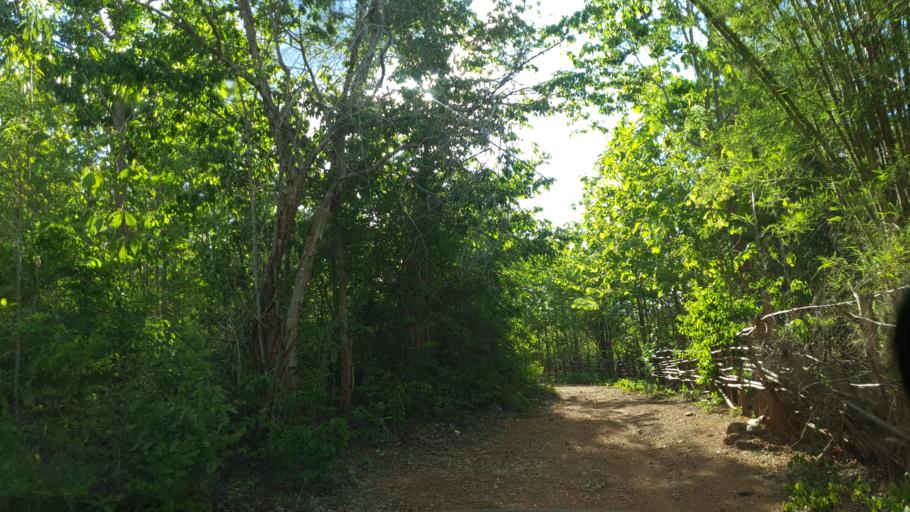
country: TH
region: Lampang
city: Sop Prap
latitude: 17.8932
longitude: 99.2840
